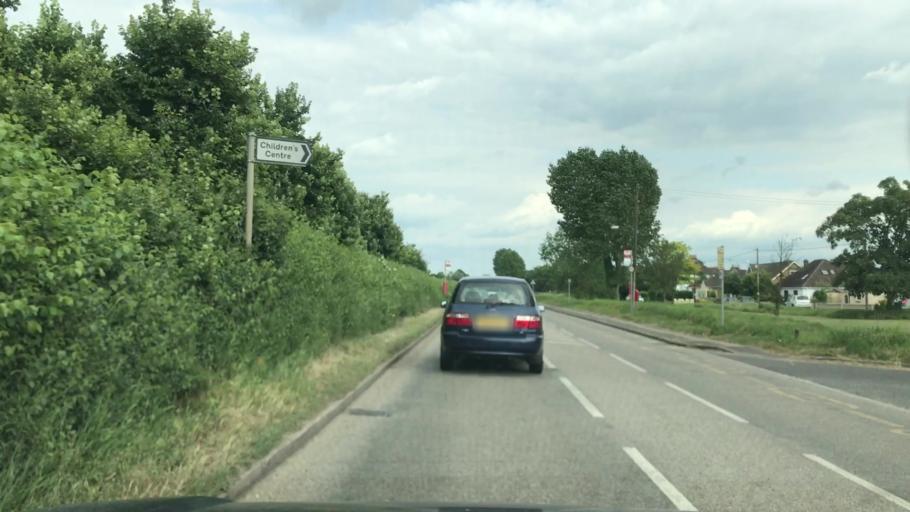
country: GB
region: England
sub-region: Kent
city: Stone
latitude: 51.4162
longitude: 0.2636
